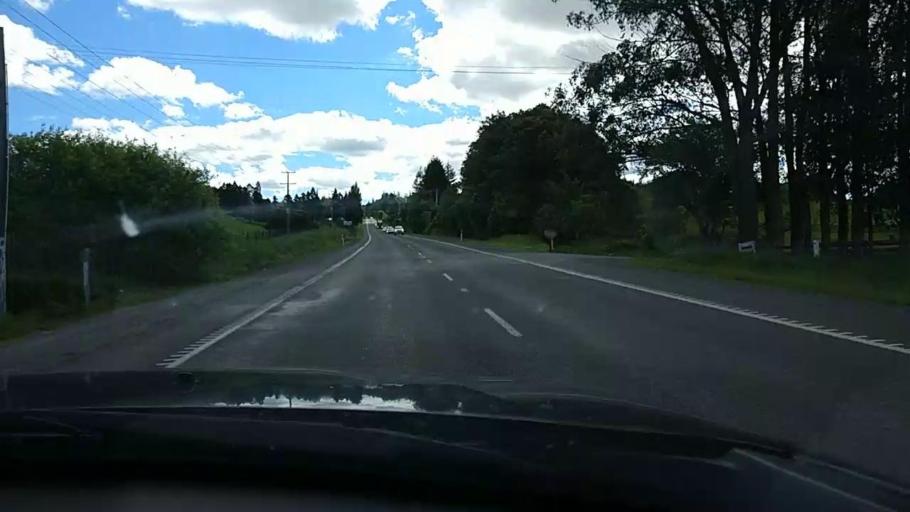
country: NZ
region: Bay of Plenty
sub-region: Rotorua District
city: Rotorua
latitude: -38.0706
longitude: 176.1415
